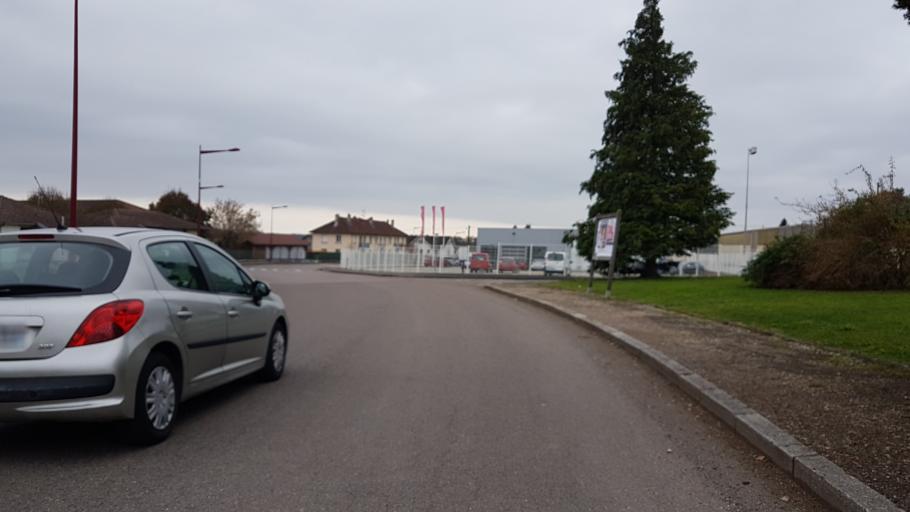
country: FR
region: Franche-Comte
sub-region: Departement de la Haute-Saone
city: Luxeuil-les-Bains
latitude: 47.8139
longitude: 6.3640
